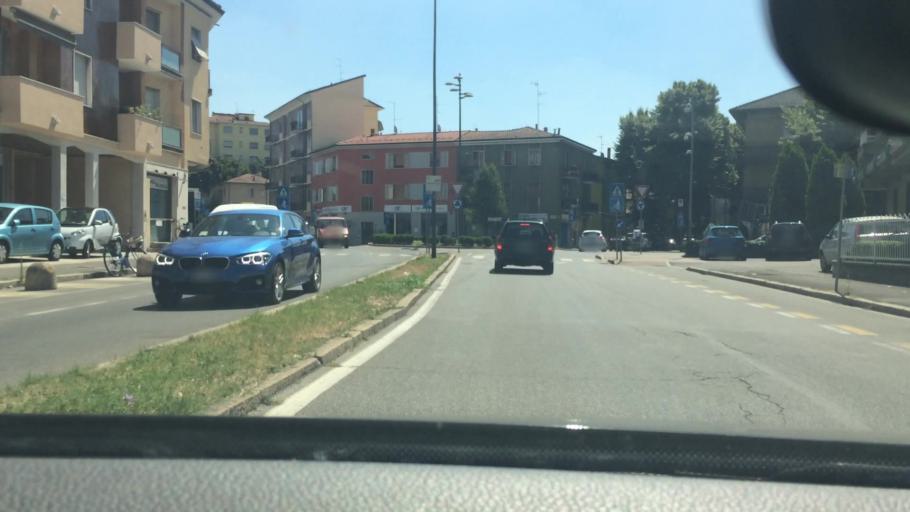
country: IT
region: Emilia-Romagna
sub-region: Provincia di Piacenza
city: Piacenza
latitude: 45.0426
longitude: 9.6787
